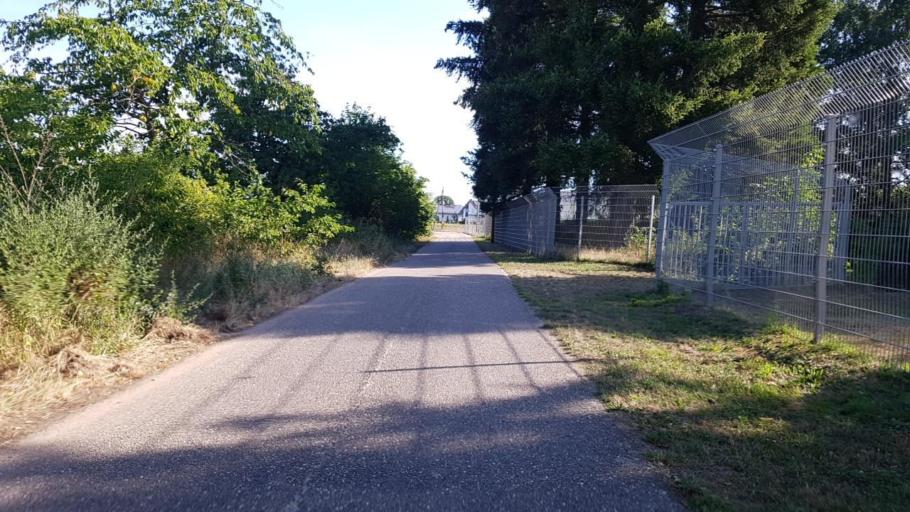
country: DE
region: Baden-Wuerttemberg
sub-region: Karlsruhe Region
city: Reilingen
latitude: 49.2912
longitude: 8.5526
